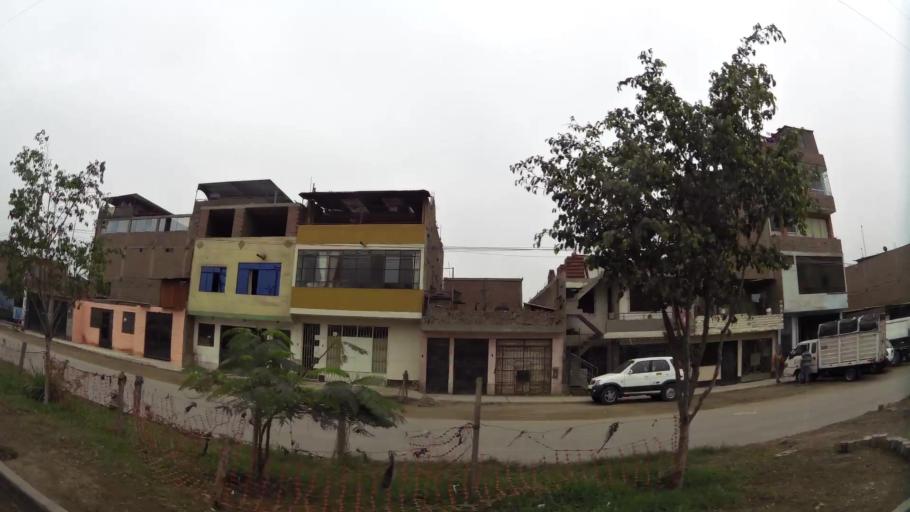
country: PE
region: Lima
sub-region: Lima
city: Independencia
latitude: -11.9421
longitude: -76.9841
